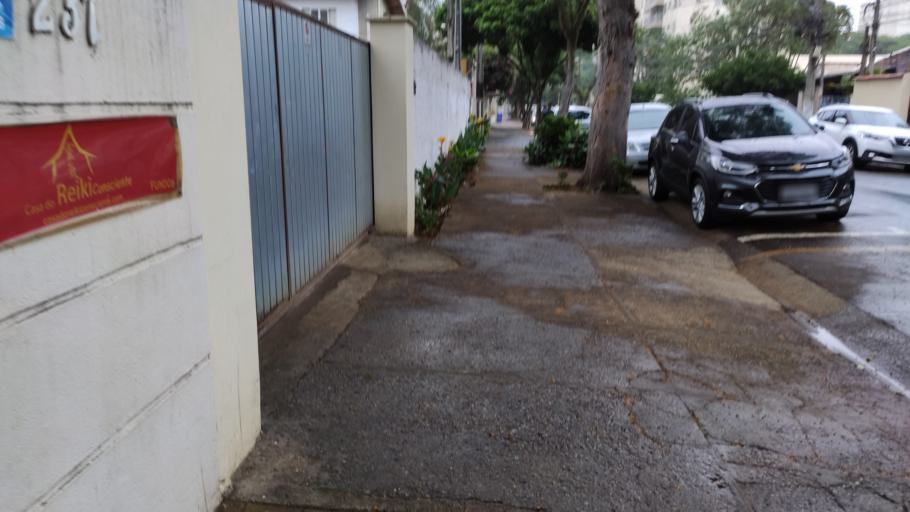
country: BR
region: Sao Paulo
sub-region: Sao Jose Dos Campos
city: Sao Jose dos Campos
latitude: -23.2047
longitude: -45.9014
